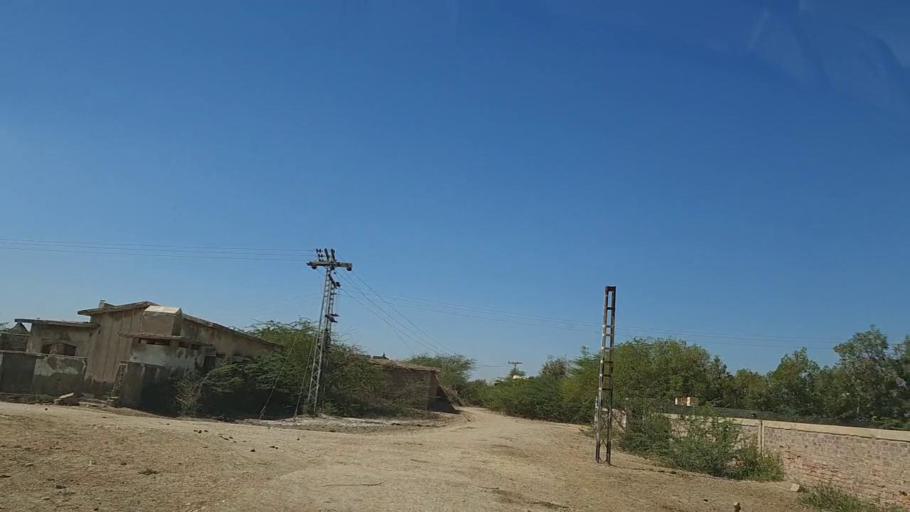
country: PK
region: Sindh
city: Dhoro Naro
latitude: 25.5159
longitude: 69.5249
